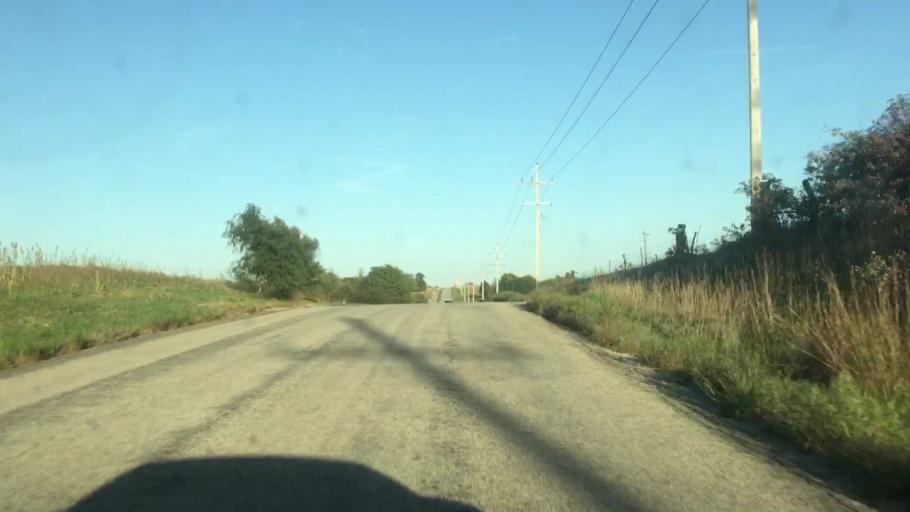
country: US
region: Kansas
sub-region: Atchison County
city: Atchison
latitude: 39.5656
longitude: -95.3297
